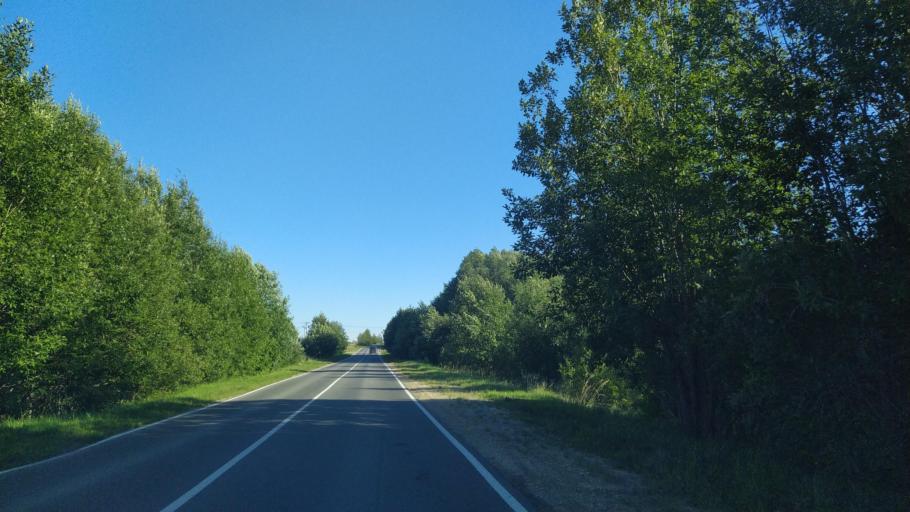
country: RU
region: Leningrad
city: Siverskiy
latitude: 59.3402
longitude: 30.0238
